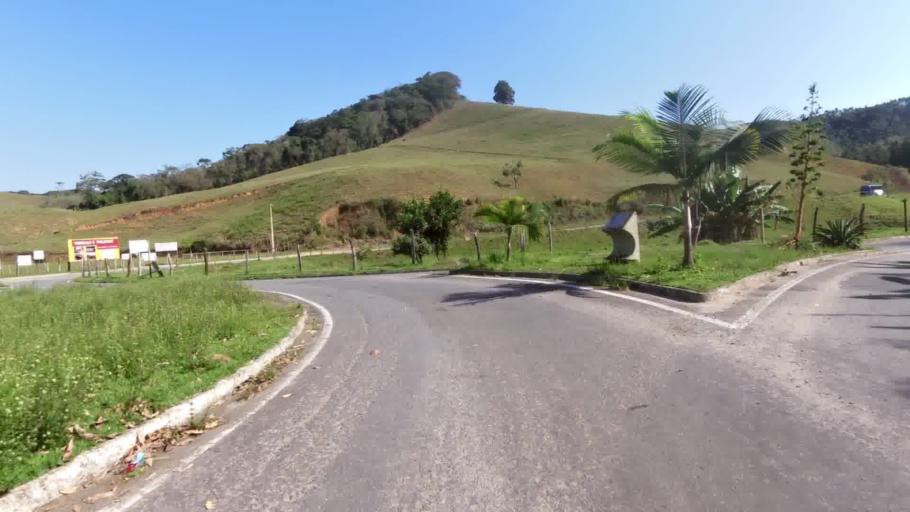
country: BR
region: Espirito Santo
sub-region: Alfredo Chaves
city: Alfredo Chaves
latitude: -20.5697
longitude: -40.8097
